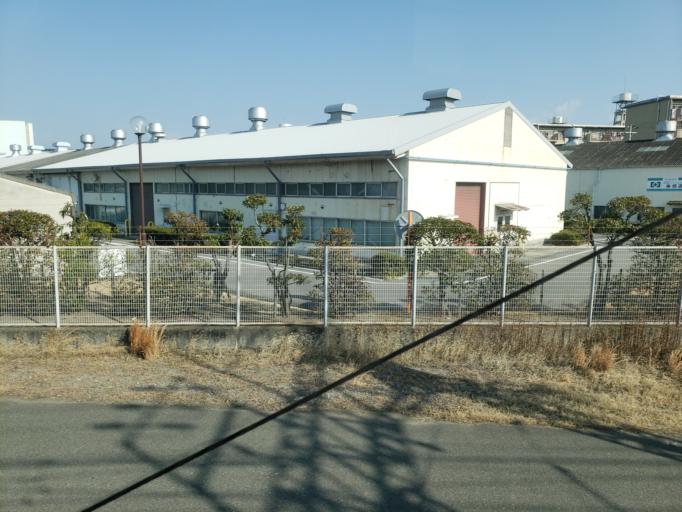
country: JP
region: Hyogo
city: Amagasaki
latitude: 34.7308
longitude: 135.4383
